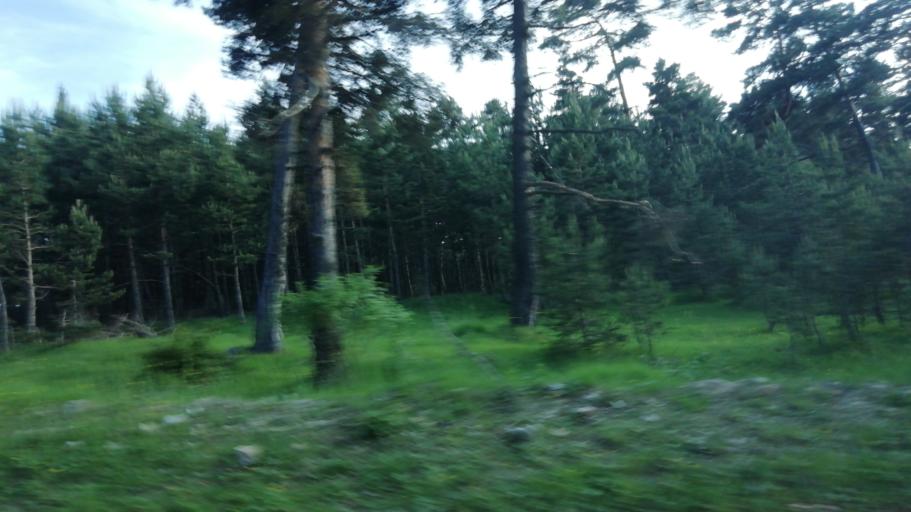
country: TR
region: Karabuk
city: Eskipazar
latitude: 41.0442
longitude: 32.5515
